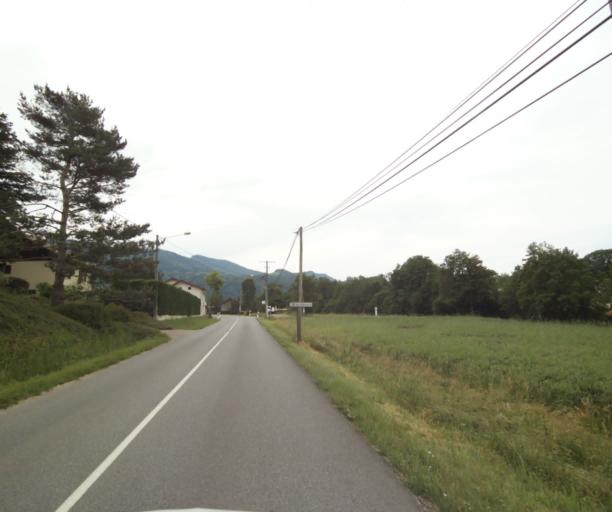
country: FR
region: Rhone-Alpes
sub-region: Departement de la Haute-Savoie
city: Allinges
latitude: 46.3244
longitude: 6.4742
